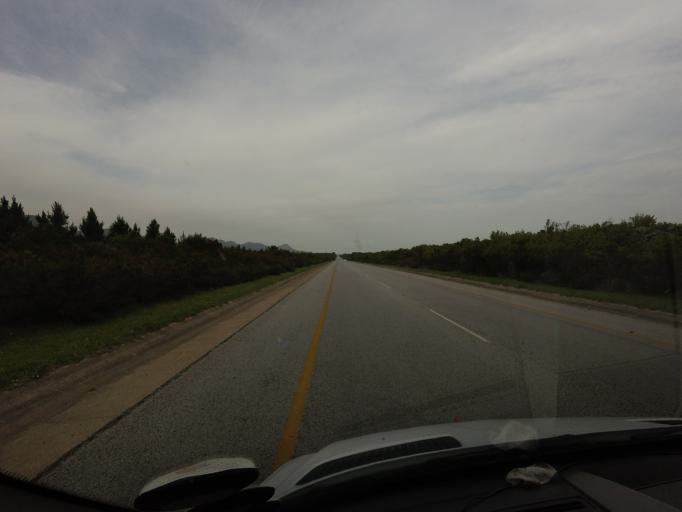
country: ZA
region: Eastern Cape
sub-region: Cacadu District Municipality
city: Kareedouw
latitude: -34.0472
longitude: 24.4186
